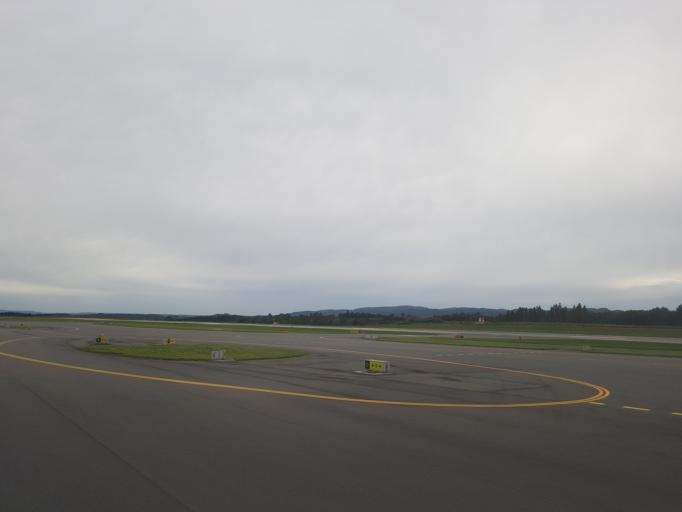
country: NO
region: Hordaland
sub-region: Bergen
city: Ytrebygda
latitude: 60.2906
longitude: 5.2233
